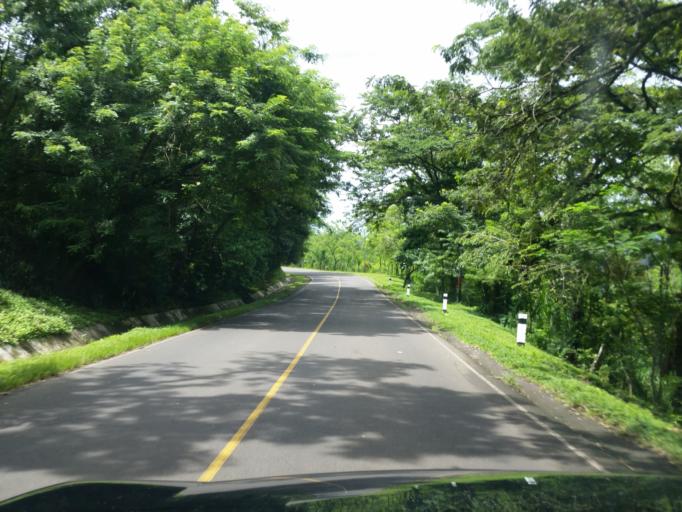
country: NI
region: Matagalpa
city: San Ramon
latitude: 13.1007
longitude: -85.7438
